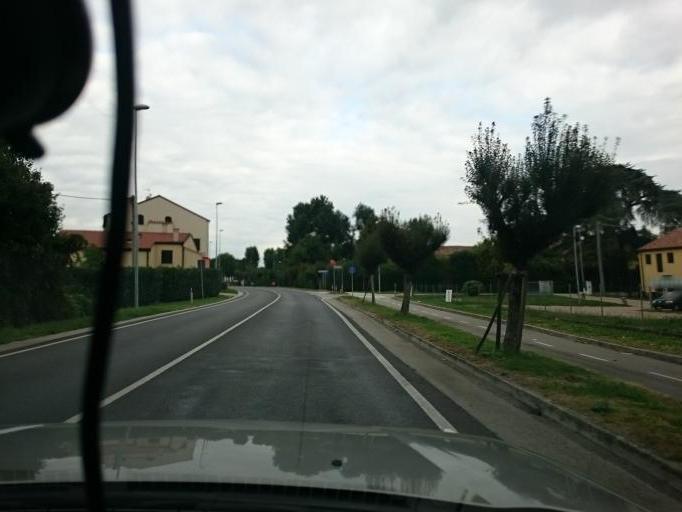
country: IT
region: Veneto
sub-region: Provincia di Padova
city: Arlesega
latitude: 45.4590
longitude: 11.7204
